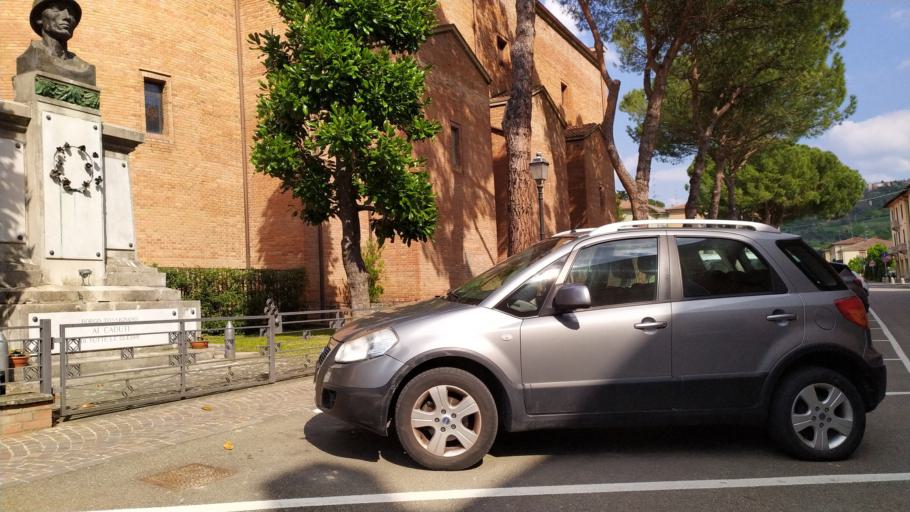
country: IT
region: Emilia-Romagna
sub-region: Provincia di Bologna
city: Borgo Tossignano
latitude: 44.2776
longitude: 11.5873
